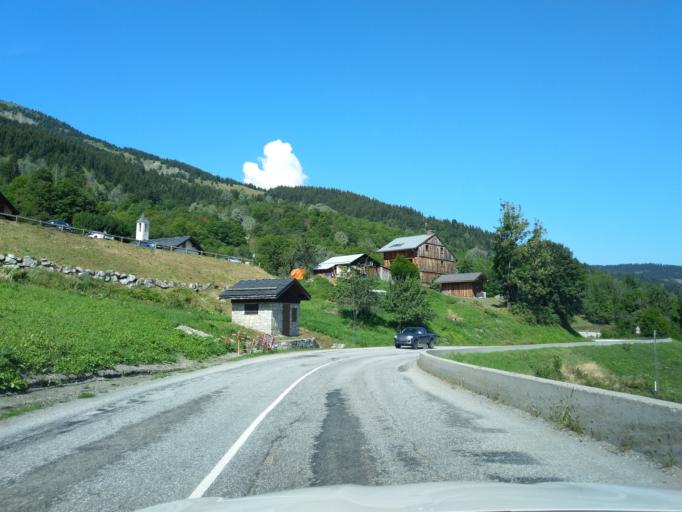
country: FR
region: Rhone-Alpes
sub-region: Departement de la Savoie
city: Meribel
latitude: 45.4197
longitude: 6.5550
